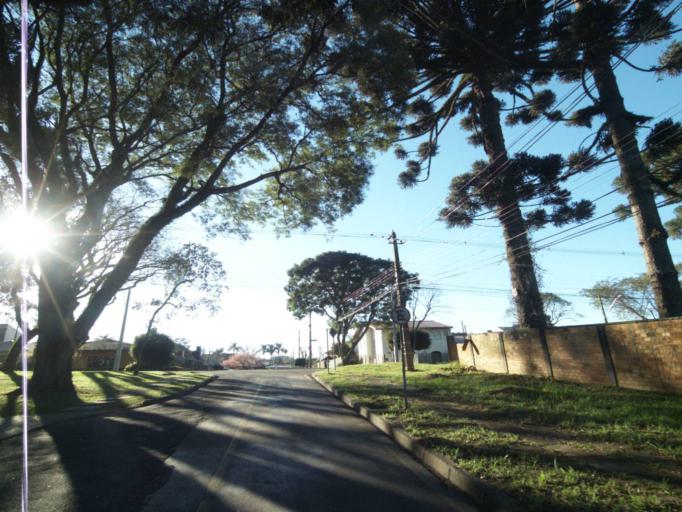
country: BR
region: Parana
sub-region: Pinhais
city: Pinhais
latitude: -25.4212
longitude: -49.2277
